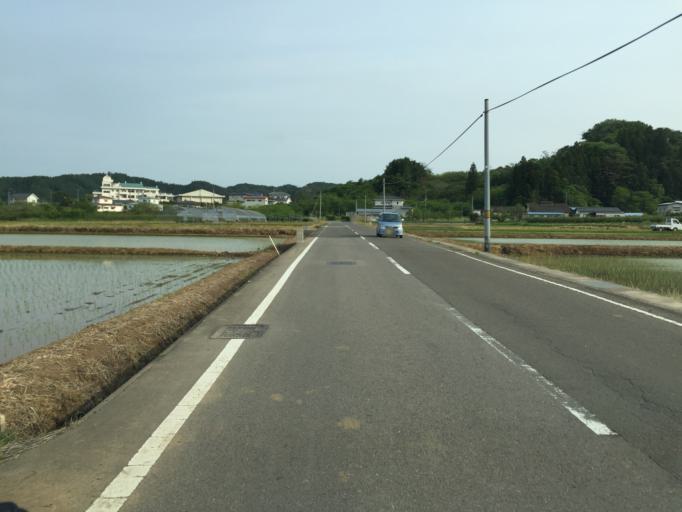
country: JP
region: Fukushima
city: Fukushima-shi
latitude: 37.7135
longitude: 140.4282
